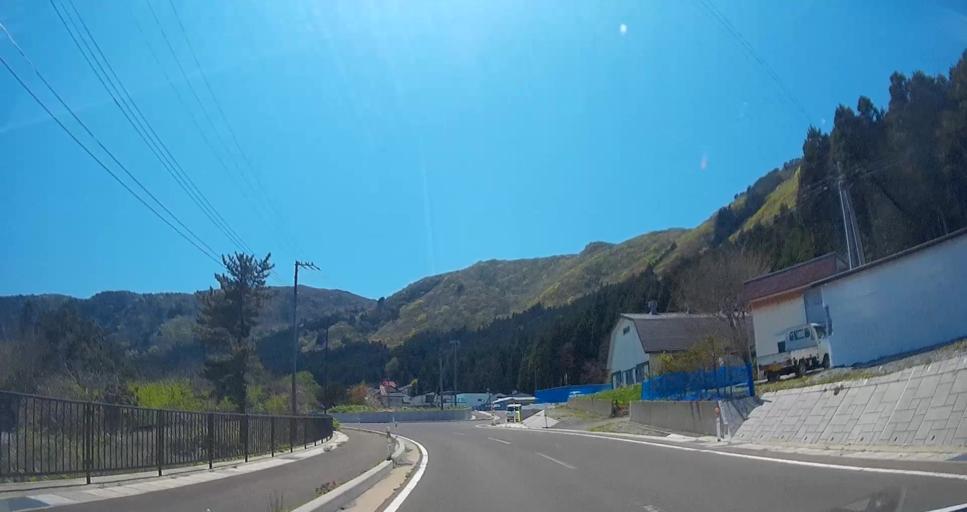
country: JP
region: Aomori
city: Mutsu
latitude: 41.4023
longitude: 141.4469
